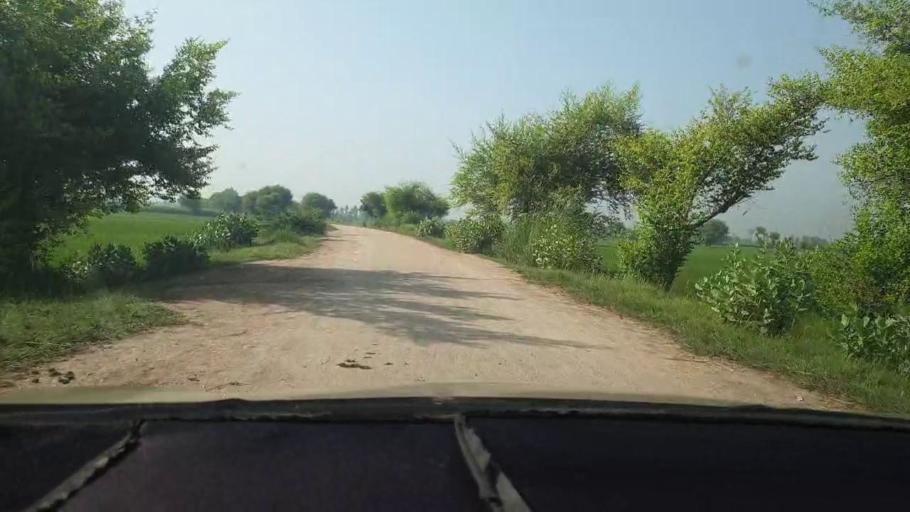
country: PK
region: Sindh
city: Kambar
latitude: 27.6184
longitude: 68.0904
